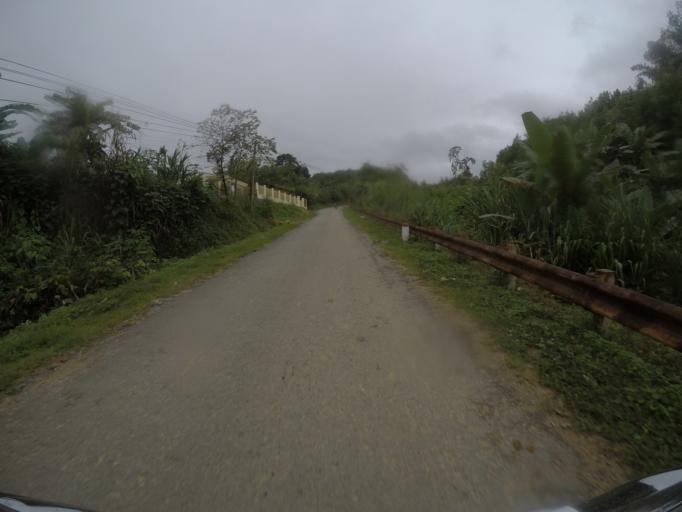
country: LA
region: Xekong
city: Dak Cheung
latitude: 15.6173
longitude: 107.5036
